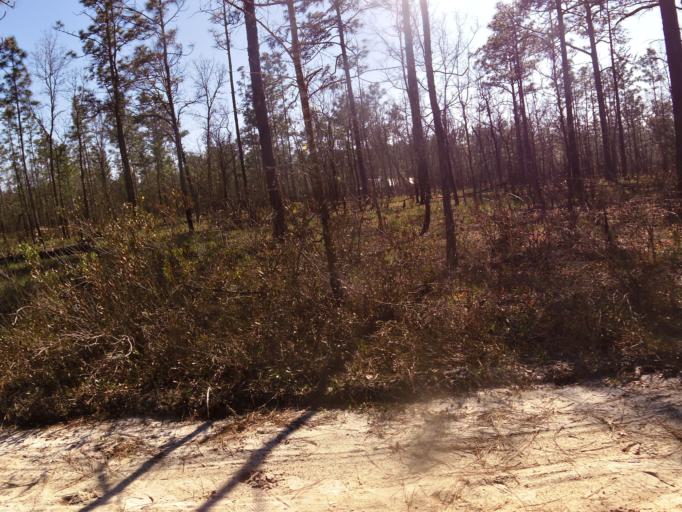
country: US
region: Florida
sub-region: Clay County
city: Middleburg
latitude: 30.1372
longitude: -81.8834
